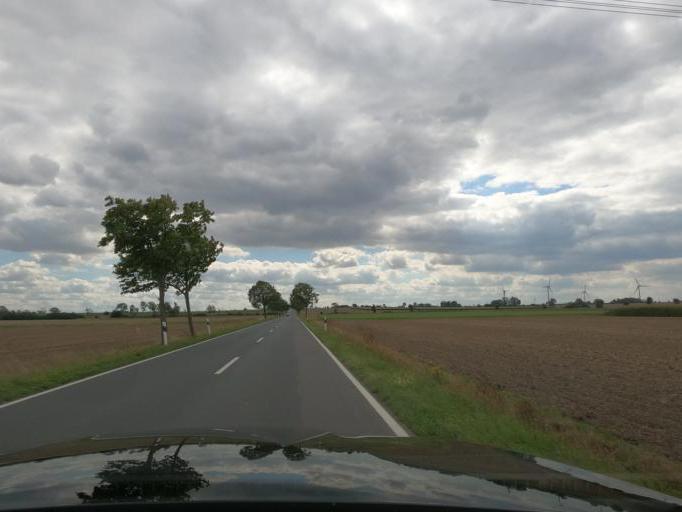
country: DE
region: Lower Saxony
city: Hohenhameln
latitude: 52.3012
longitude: 10.0445
